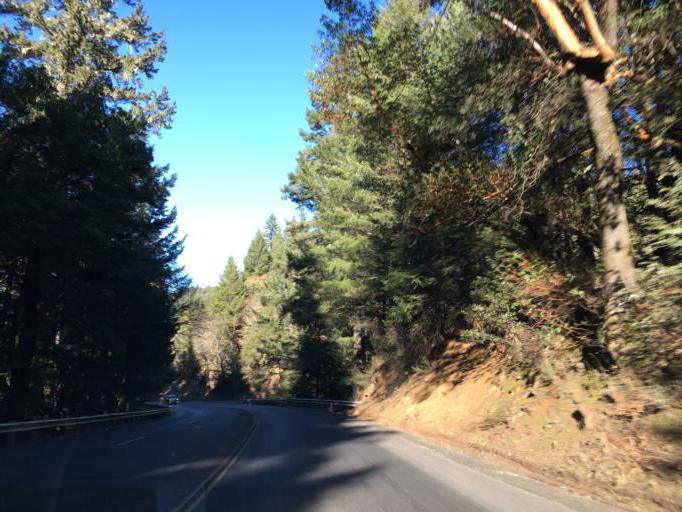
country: US
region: California
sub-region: Mendocino County
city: Laytonville
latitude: 39.7906
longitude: -123.5429
